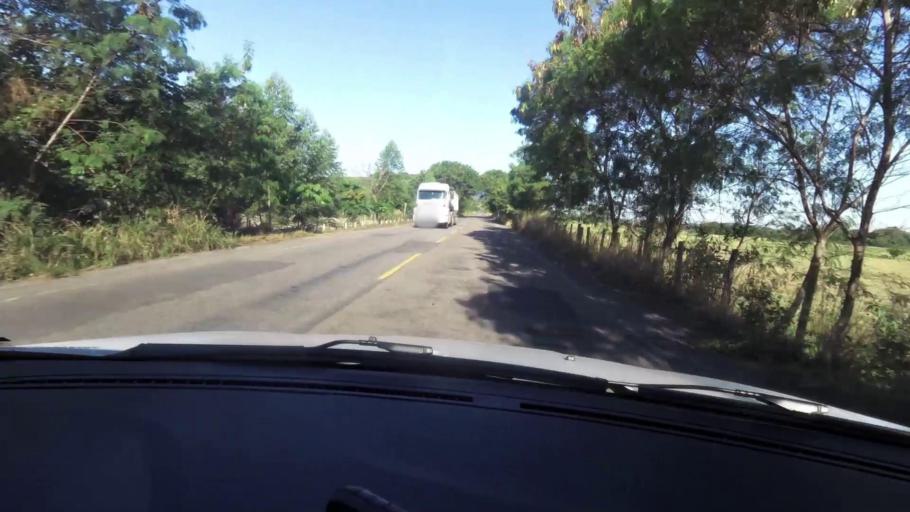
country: BR
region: Espirito Santo
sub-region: Alfredo Chaves
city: Alfredo Chaves
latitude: -20.7137
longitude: -40.6671
